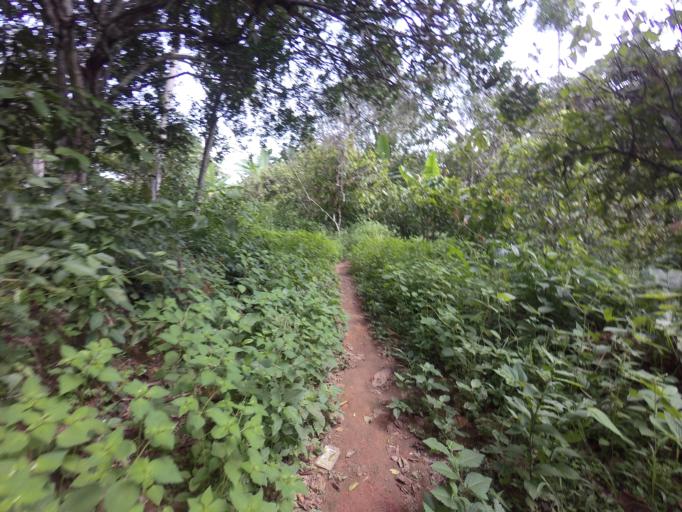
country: SL
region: Eastern Province
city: Tombodu
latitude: 8.1580
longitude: -10.6290
